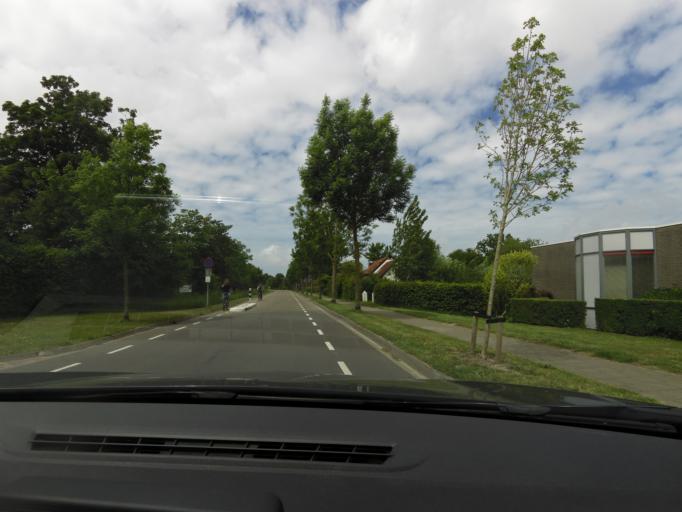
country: NL
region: Zeeland
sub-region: Schouwen-Duiveland
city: Scharendijke
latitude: 51.7364
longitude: 3.8390
